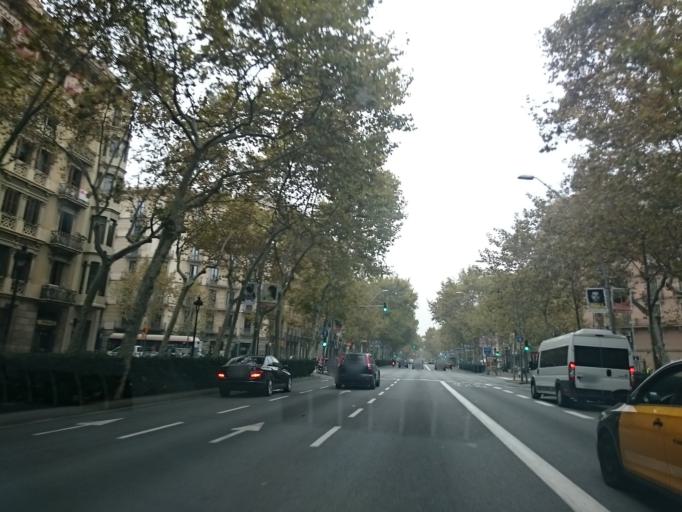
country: ES
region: Catalonia
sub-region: Provincia de Barcelona
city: Barcelona
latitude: 41.3835
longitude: 2.1604
